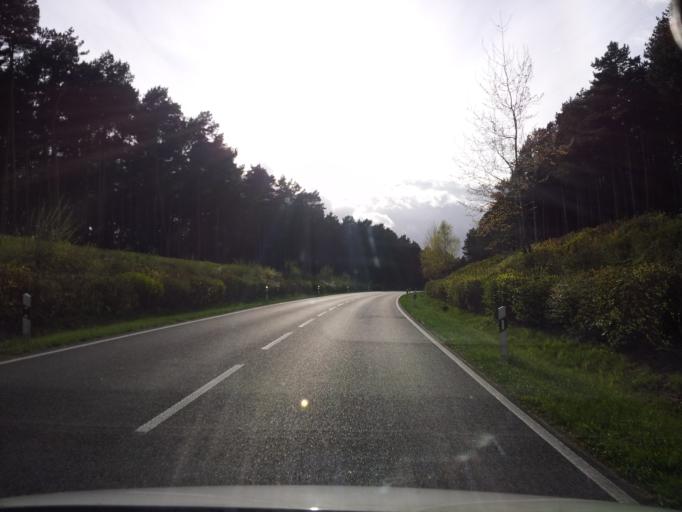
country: DE
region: Brandenburg
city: Schenkendobern
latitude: 51.8936
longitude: 14.6346
